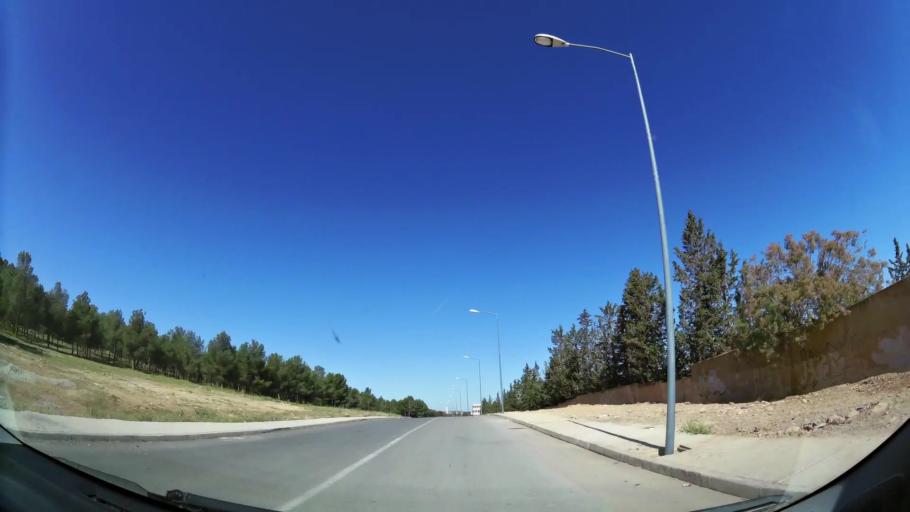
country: MA
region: Oriental
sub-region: Oujda-Angad
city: Oujda
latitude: 34.6479
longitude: -1.8939
